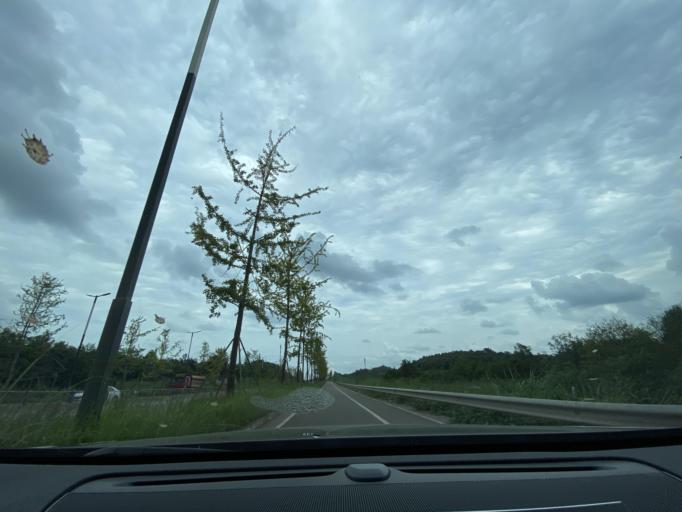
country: CN
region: Sichuan
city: Jiancheng
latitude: 30.4896
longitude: 104.4719
